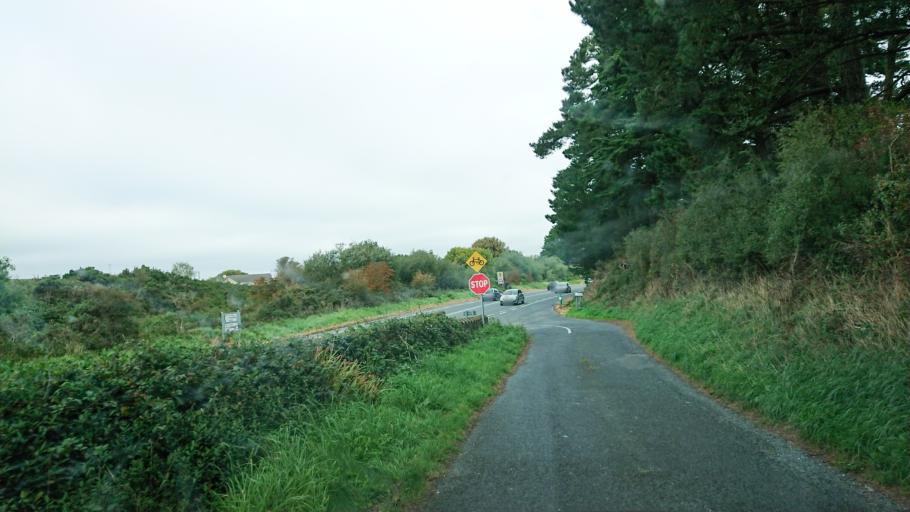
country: IE
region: Munster
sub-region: Waterford
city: Tra Mhor
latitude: 52.1937
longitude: -7.1243
